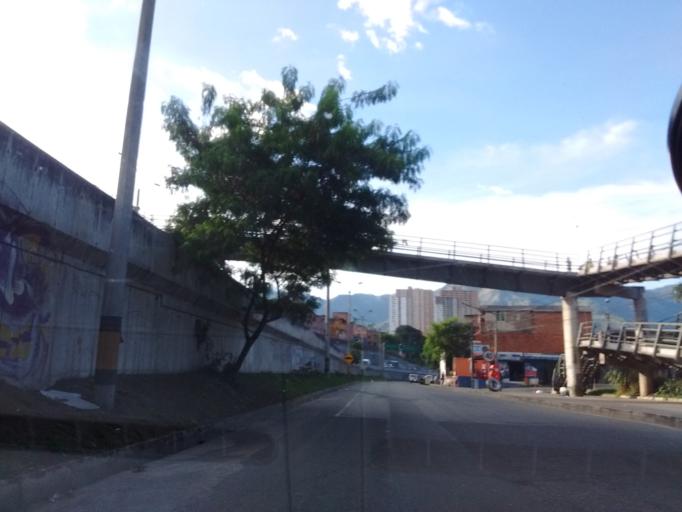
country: CO
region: Antioquia
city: Bello
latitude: 6.3072
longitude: -75.5582
